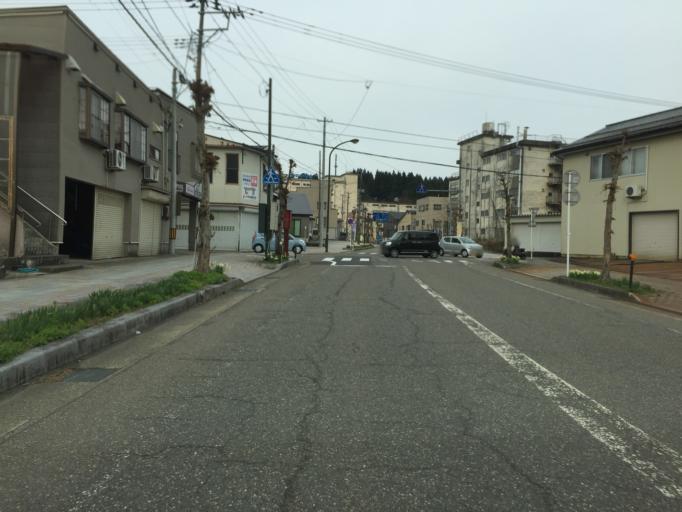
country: JP
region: Niigata
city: Tochio-honcho
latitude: 37.4743
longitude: 138.9974
